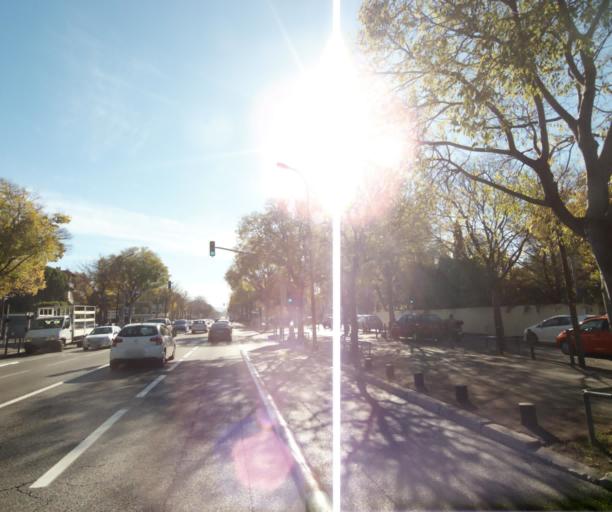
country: FR
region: Provence-Alpes-Cote d'Azur
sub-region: Departement des Bouches-du-Rhone
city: Marseille 09
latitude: 43.2592
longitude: 5.3988
